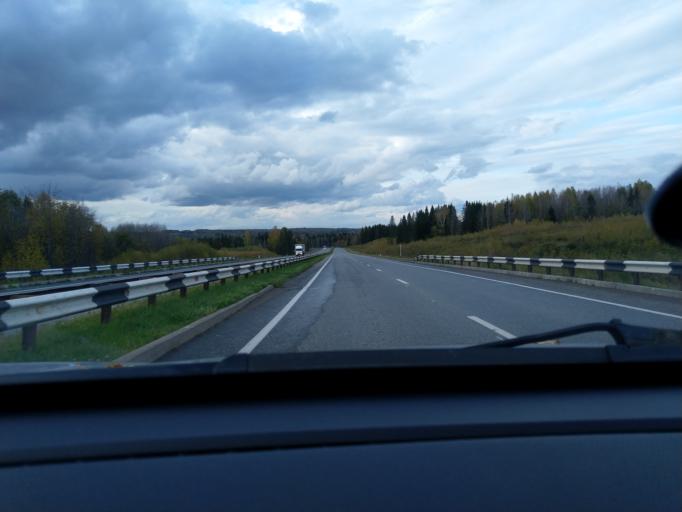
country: RU
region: Perm
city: Polazna
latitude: 58.3019
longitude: 56.4842
